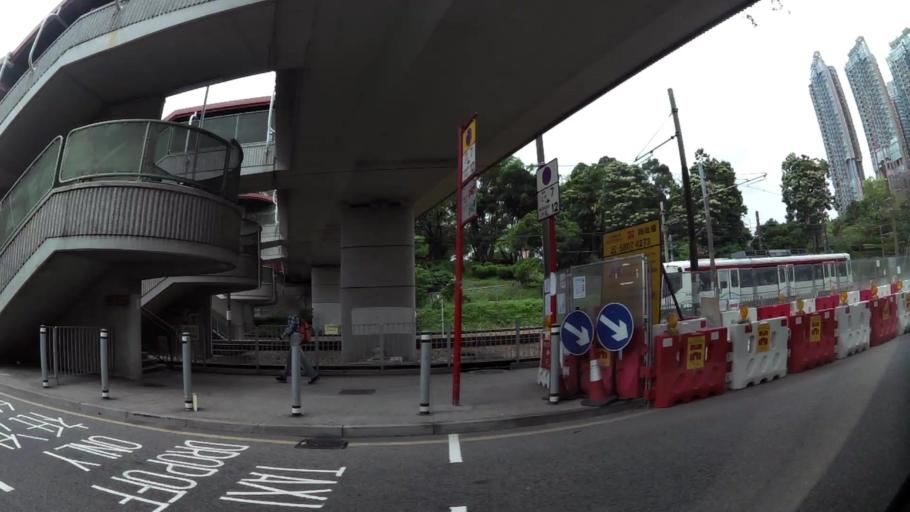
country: HK
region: Tuen Mun
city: Tuen Mun
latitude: 22.3918
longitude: 113.9751
